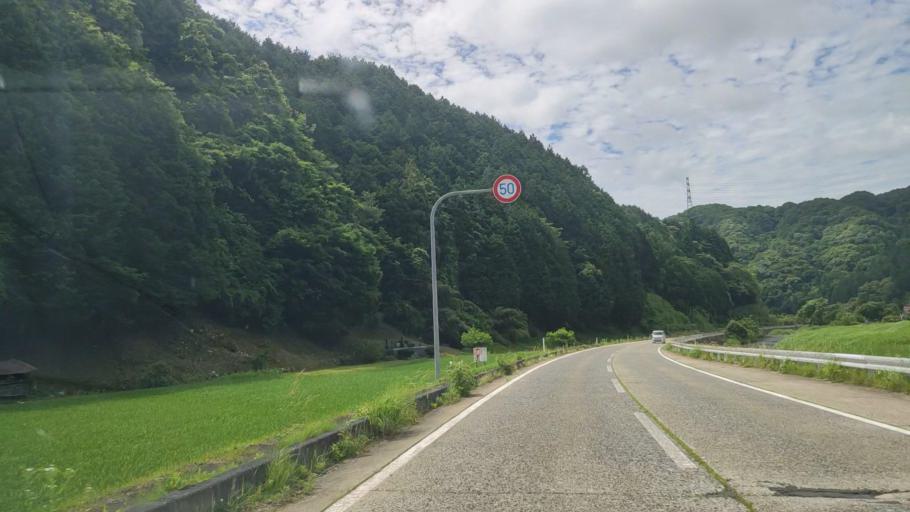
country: JP
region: Okayama
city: Niimi
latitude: 35.1682
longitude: 133.5799
